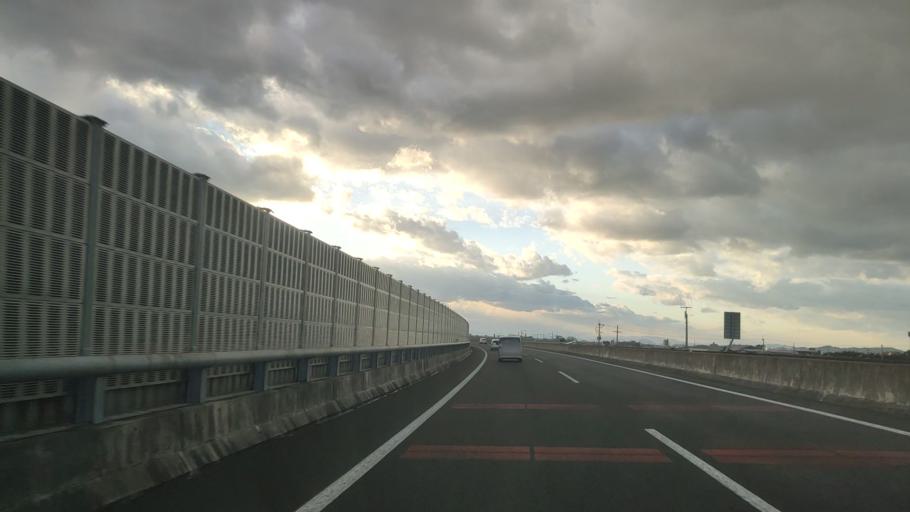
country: JP
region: Ehime
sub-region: Shikoku-chuo Shi
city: Matsuyama
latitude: 33.7887
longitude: 132.8256
